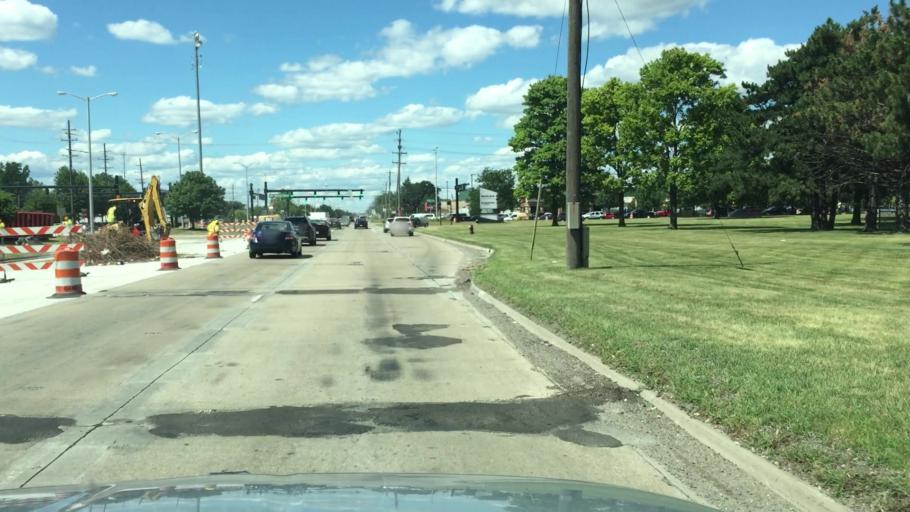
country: US
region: Michigan
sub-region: Macomb County
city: Sterling Heights
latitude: 42.5638
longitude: -83.0489
